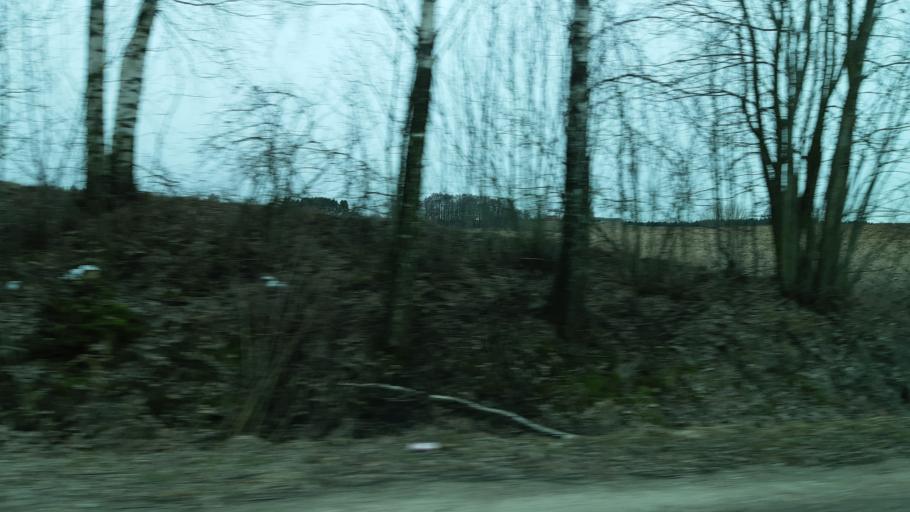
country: PL
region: Podlasie
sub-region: Suwalki
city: Suwalki
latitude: 54.3313
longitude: 22.9482
